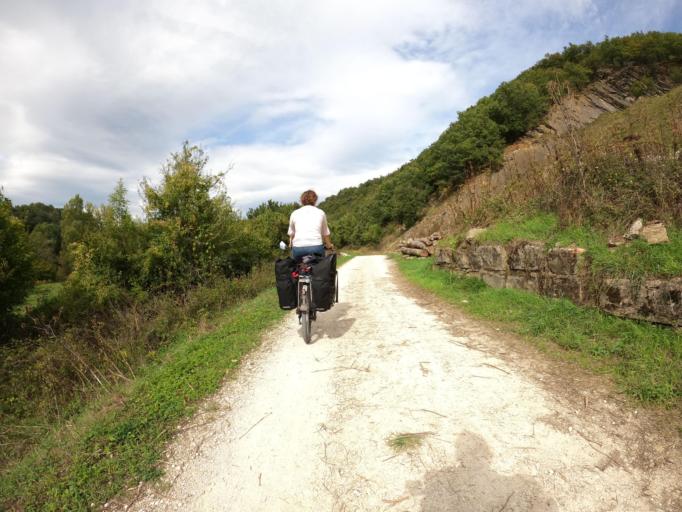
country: ES
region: Navarre
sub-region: Provincia de Navarra
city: Irurtzun
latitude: 42.9589
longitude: -1.8241
